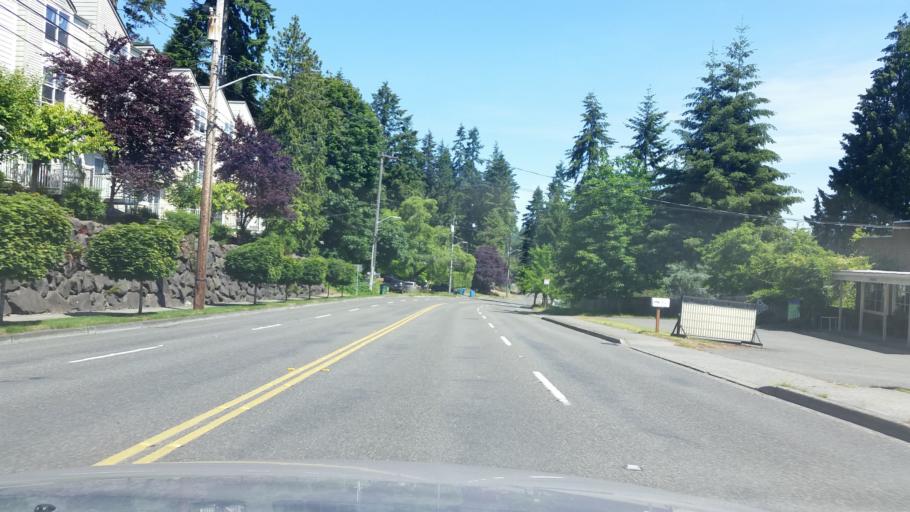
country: US
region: Washington
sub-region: Snohomish County
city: Mountlake Terrace
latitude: 47.7676
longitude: -122.3145
